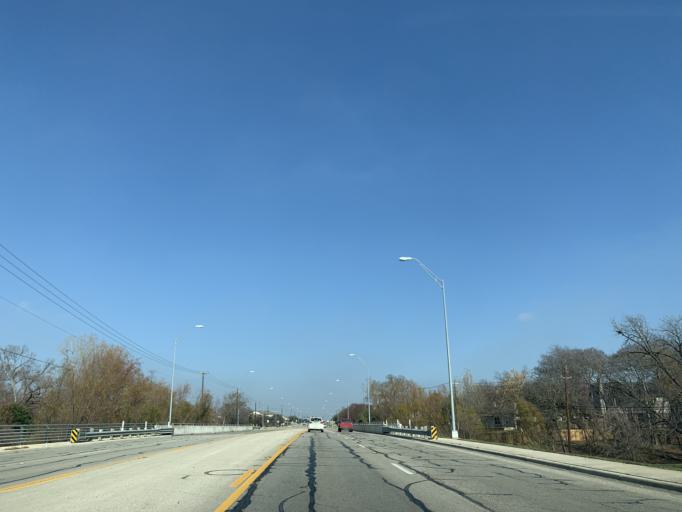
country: US
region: Texas
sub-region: Williamson County
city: Round Rock
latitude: 30.5349
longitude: -97.6520
